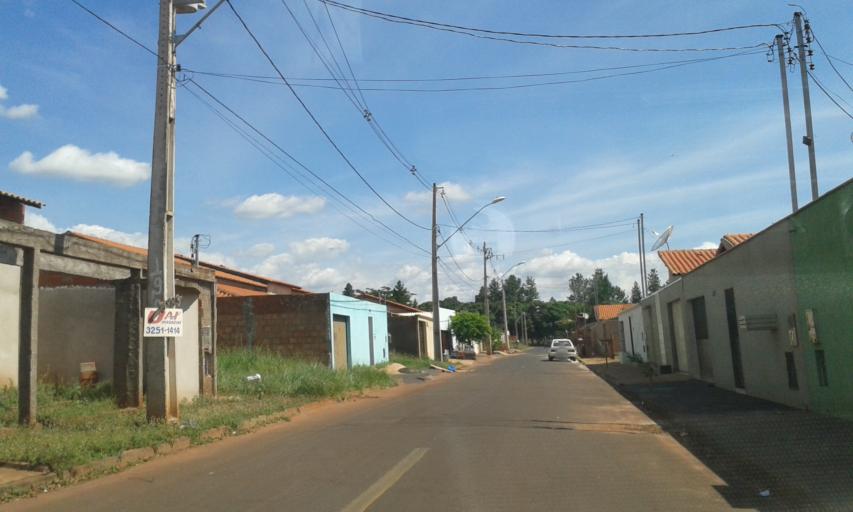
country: BR
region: Minas Gerais
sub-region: Santa Vitoria
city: Santa Vitoria
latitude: -18.8547
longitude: -50.1279
